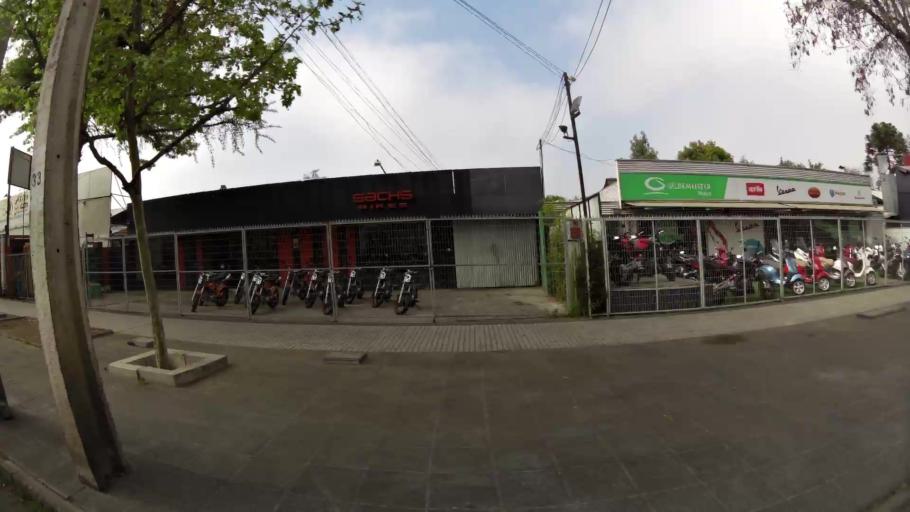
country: CL
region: Santiago Metropolitan
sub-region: Provincia de Santiago
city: Villa Presidente Frei, Nunoa, Santiago, Chile
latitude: -33.3819
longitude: -70.5458
